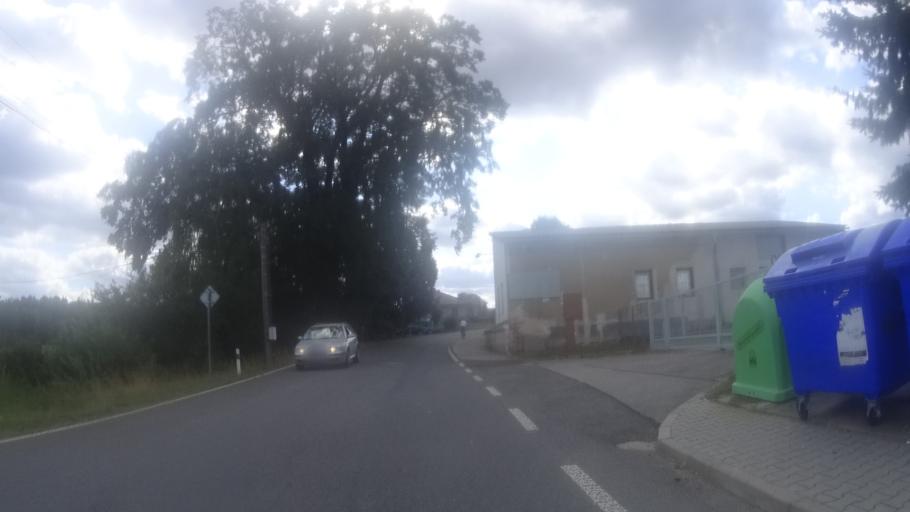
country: CZ
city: Borohradek
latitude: 50.0756
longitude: 16.1301
